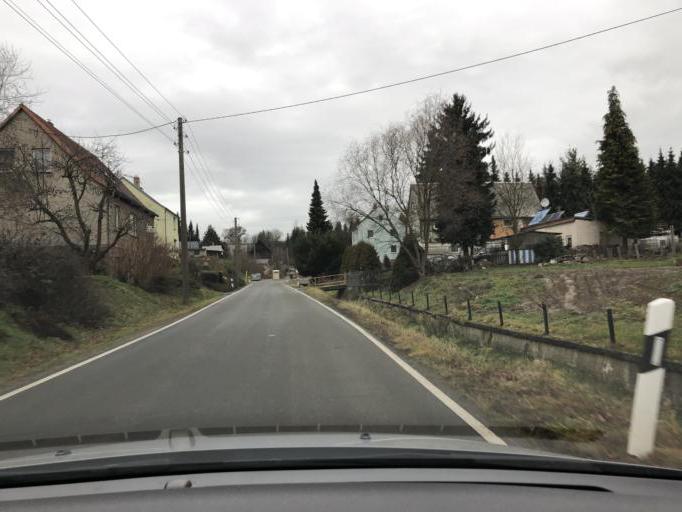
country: DE
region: Saxony
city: Rosswein
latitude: 51.0734
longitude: 13.2380
